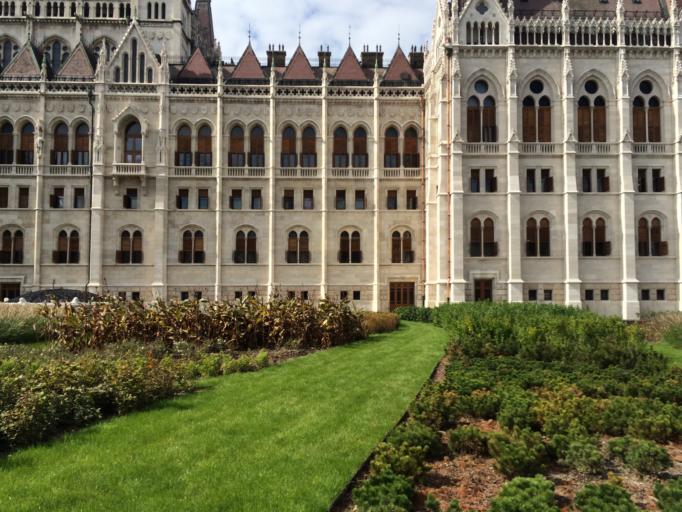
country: HU
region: Budapest
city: Budapest
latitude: 47.5079
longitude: 19.0468
